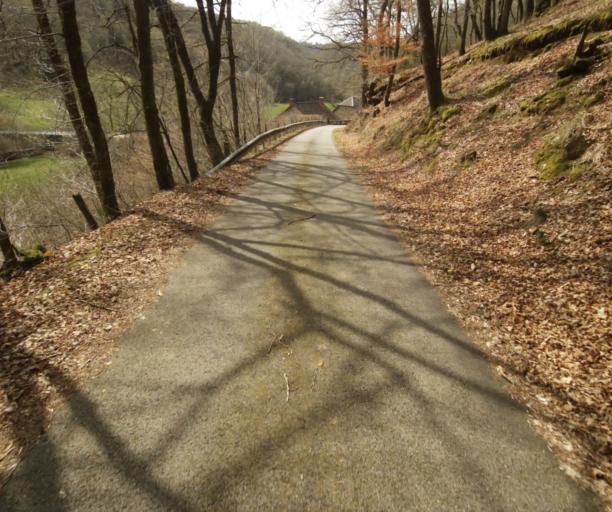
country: FR
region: Limousin
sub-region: Departement de la Correze
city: Naves
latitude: 45.3416
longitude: 1.8010
